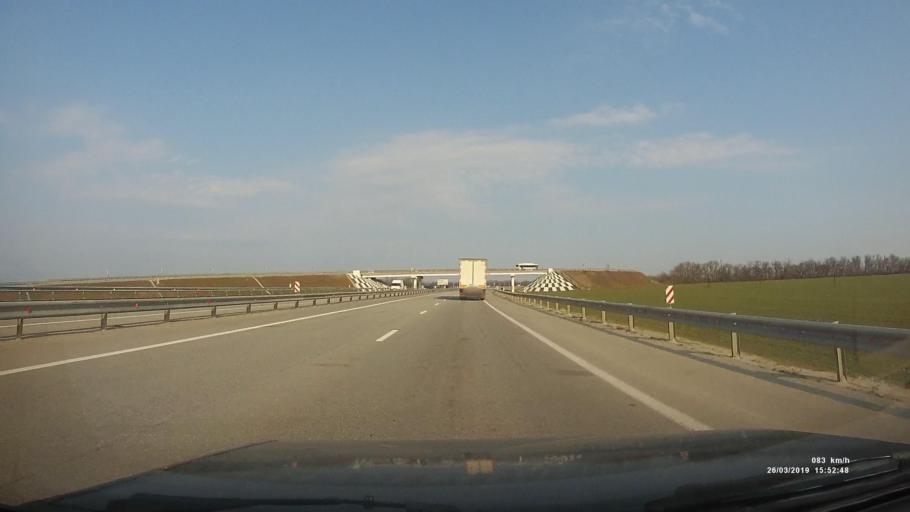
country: RU
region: Rostov
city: Krym
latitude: 47.2724
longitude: 39.5294
